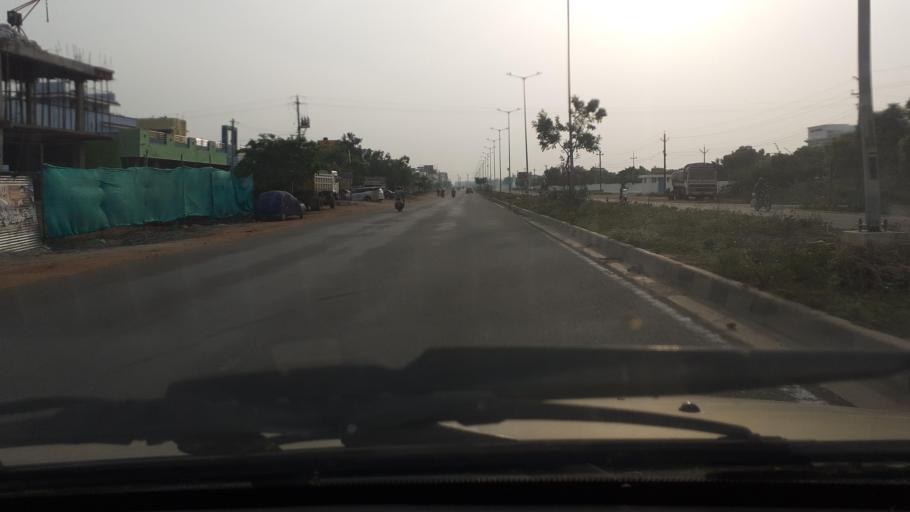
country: IN
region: Tamil Nadu
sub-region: Tirunelveli Kattabo
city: Tirunelveli
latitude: 8.7138
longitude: 77.7874
